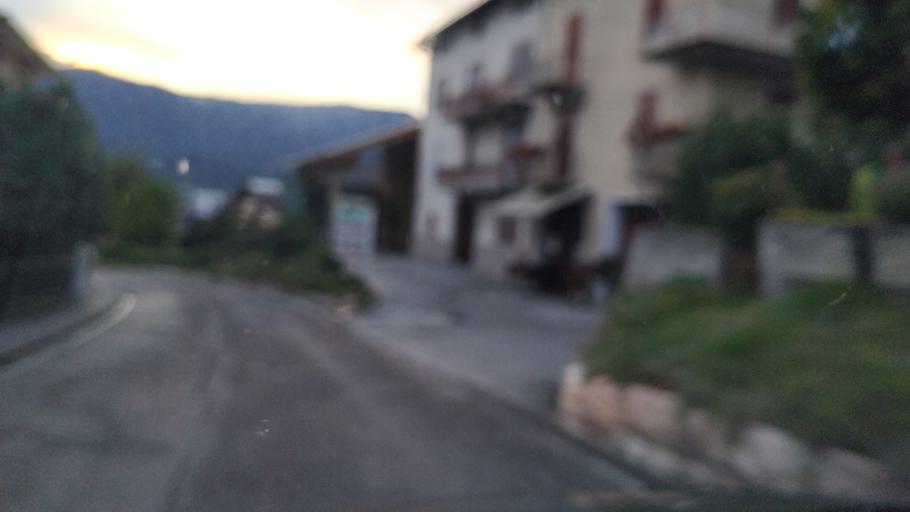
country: IT
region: Trentino-Alto Adige
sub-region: Provincia di Trento
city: Fondo
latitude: 46.4409
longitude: 11.1323
